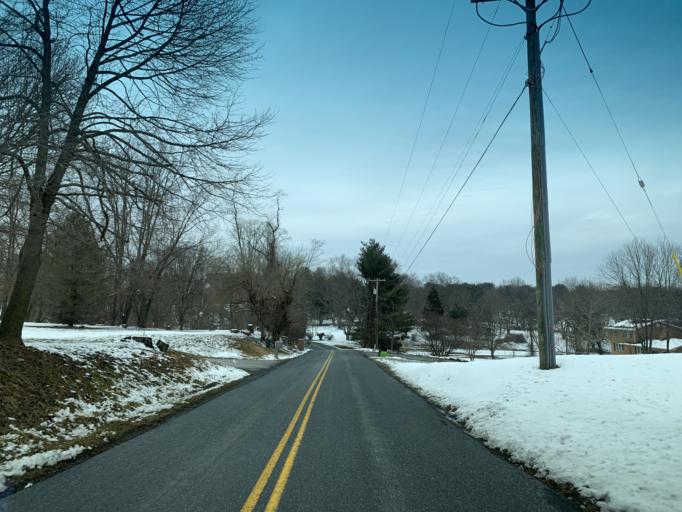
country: US
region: Maryland
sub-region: Harford County
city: Jarrettsville
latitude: 39.5813
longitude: -76.4740
